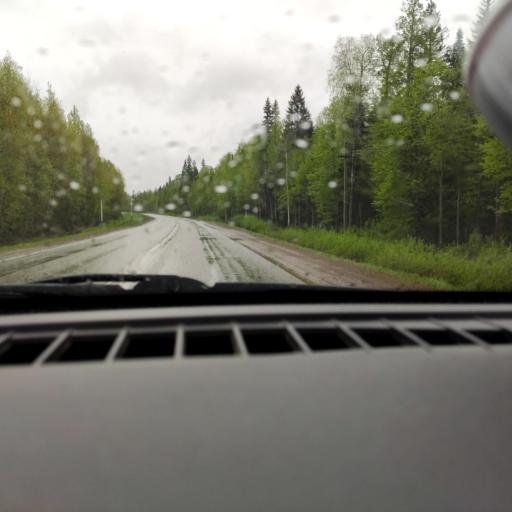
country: RU
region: Perm
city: Perm
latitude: 58.2199
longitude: 56.1682
